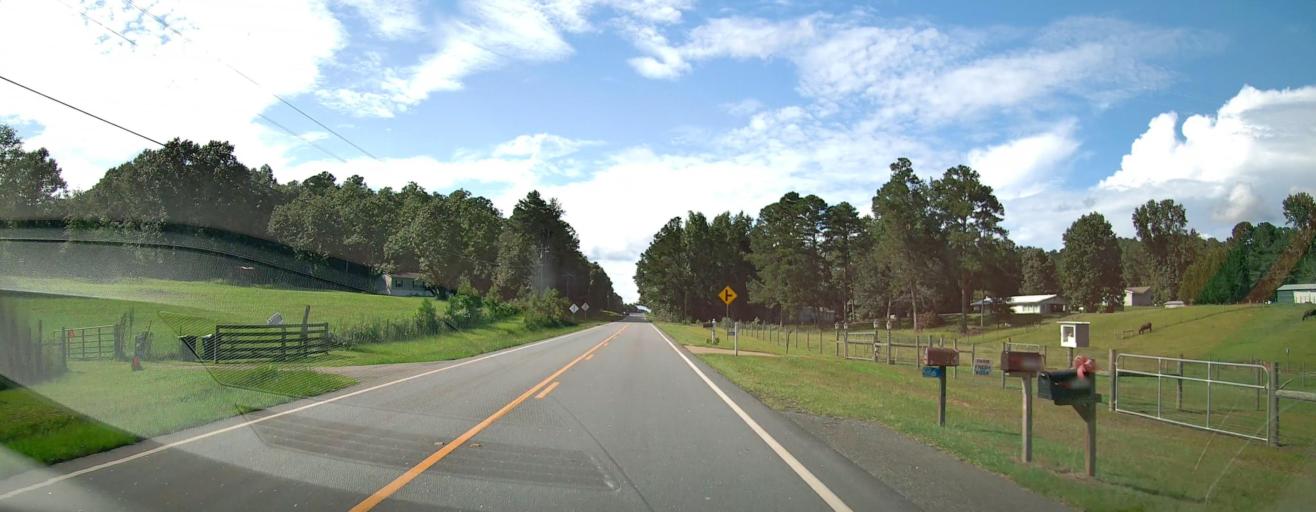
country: US
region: Georgia
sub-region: Upson County
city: Hannahs Mill
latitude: 32.9344
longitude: -84.4491
